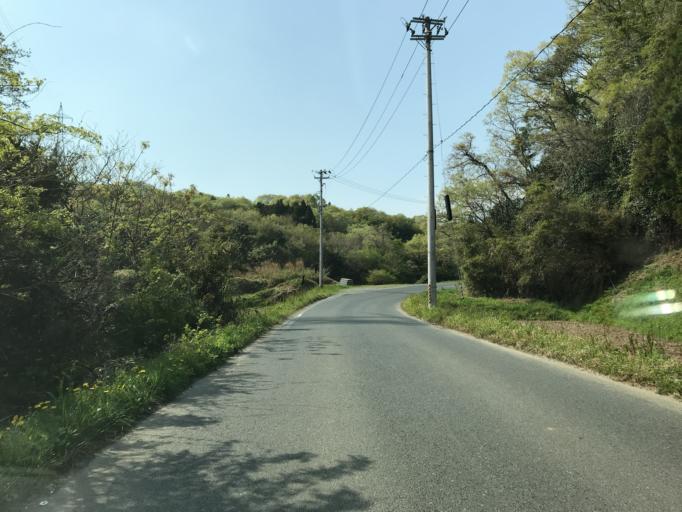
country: JP
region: Fukushima
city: Iwaki
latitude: 36.9746
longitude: 140.7633
